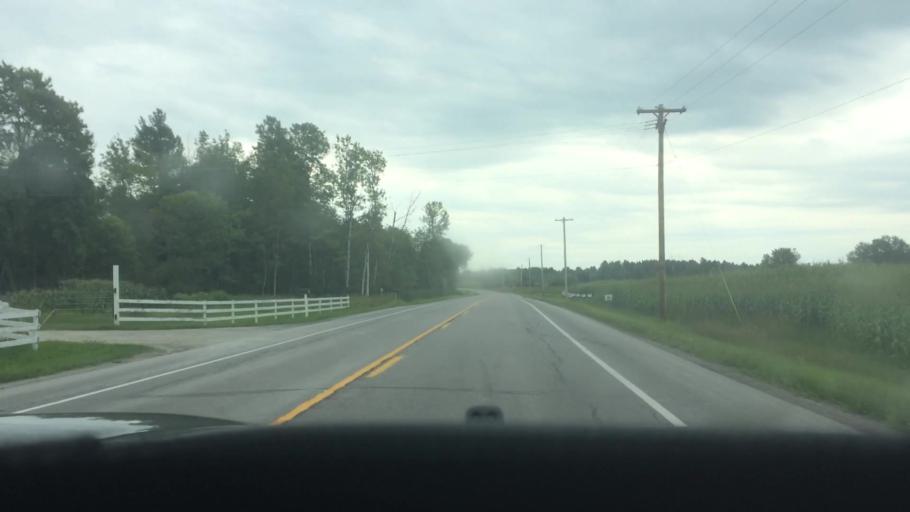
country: US
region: New York
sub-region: St. Lawrence County
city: Ogdensburg
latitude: 44.5826
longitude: -75.3706
